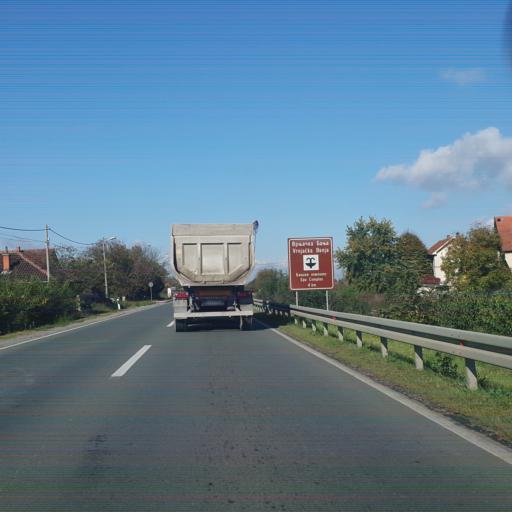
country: RS
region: Central Serbia
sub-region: Raski Okrug
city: Vrnjacka Banja
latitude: 43.6345
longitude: 20.9405
